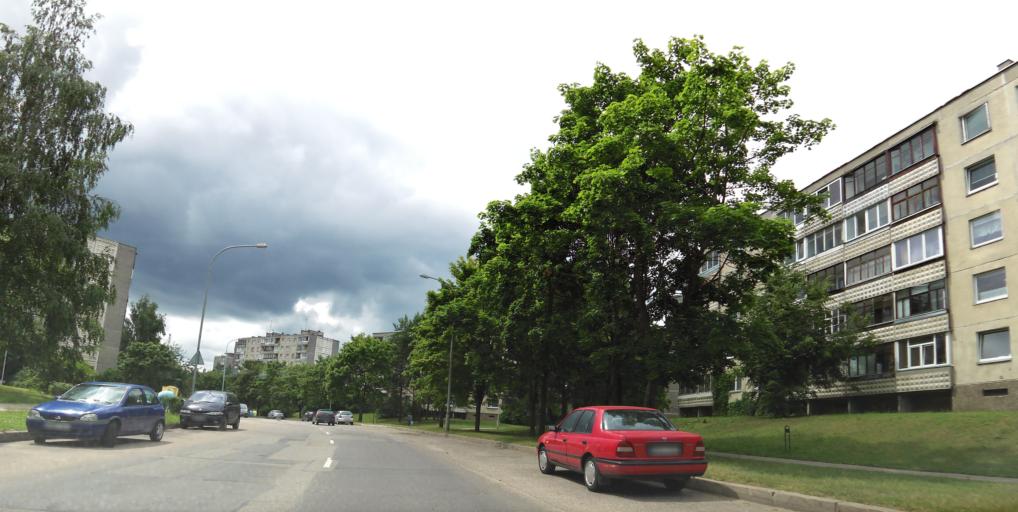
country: LT
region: Vilnius County
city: Justiniskes
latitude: 54.7126
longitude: 25.2251
